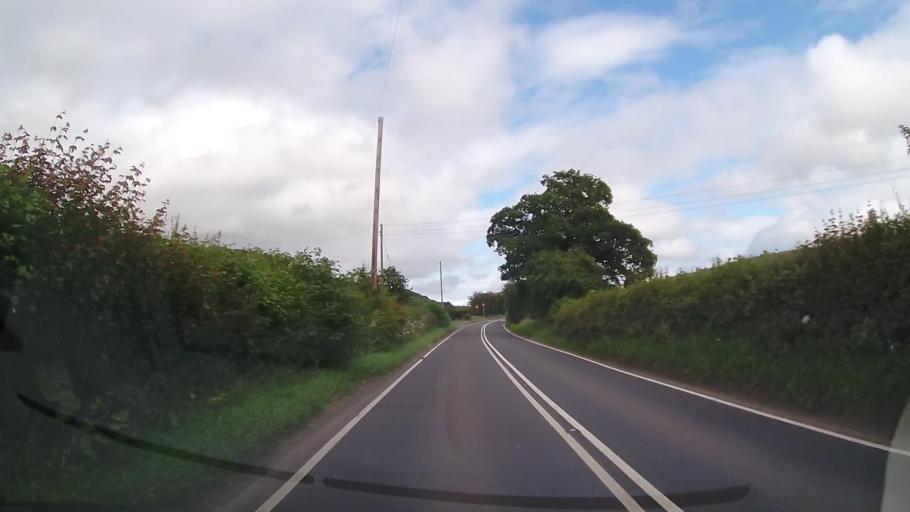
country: GB
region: England
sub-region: Shropshire
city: Pant
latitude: 52.8040
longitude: -3.1059
